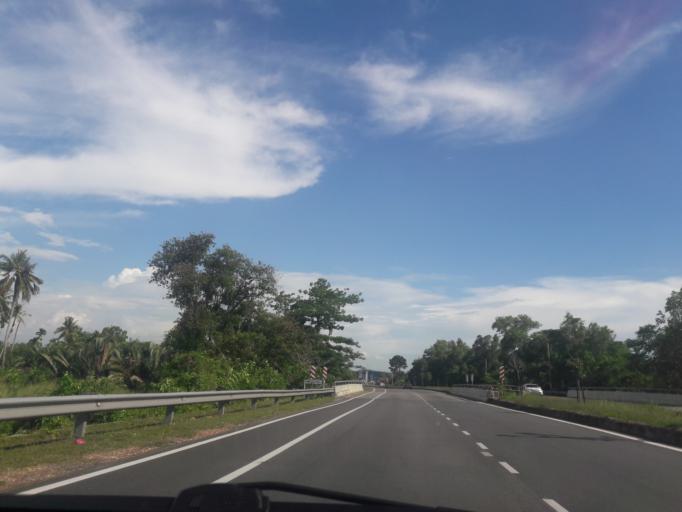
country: MY
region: Kedah
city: Sungai Petani
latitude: 5.6212
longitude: 100.4648
